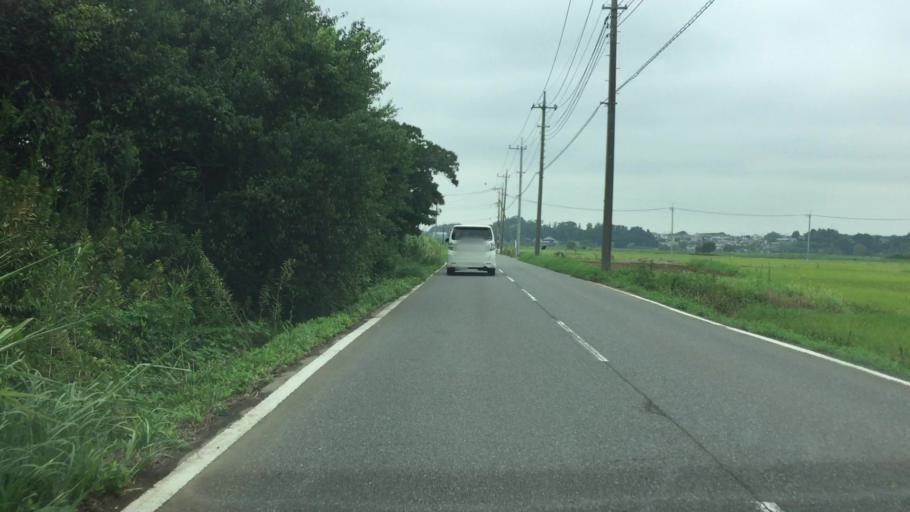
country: JP
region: Chiba
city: Abiko
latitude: 35.8532
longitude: 140.0440
